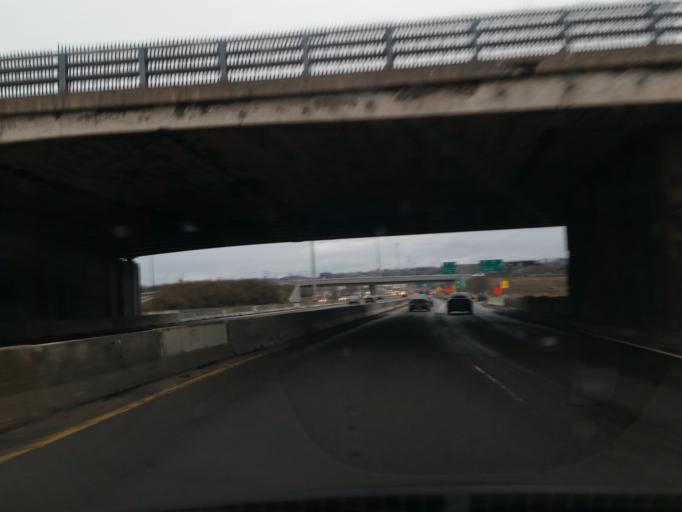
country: CA
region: Quebec
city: Quebec
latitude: 46.8369
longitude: -71.2636
